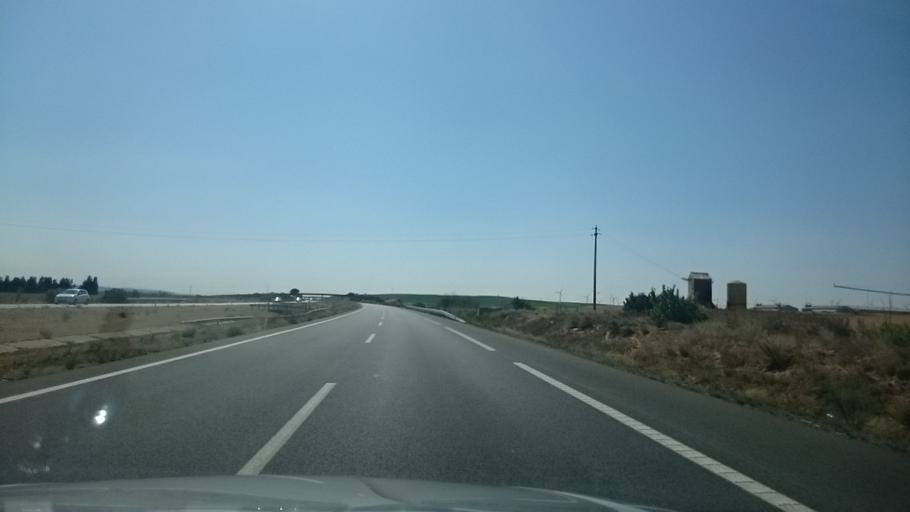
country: ES
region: Aragon
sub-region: Provincia de Zaragoza
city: Boquineni
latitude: 41.8206
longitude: -1.2878
